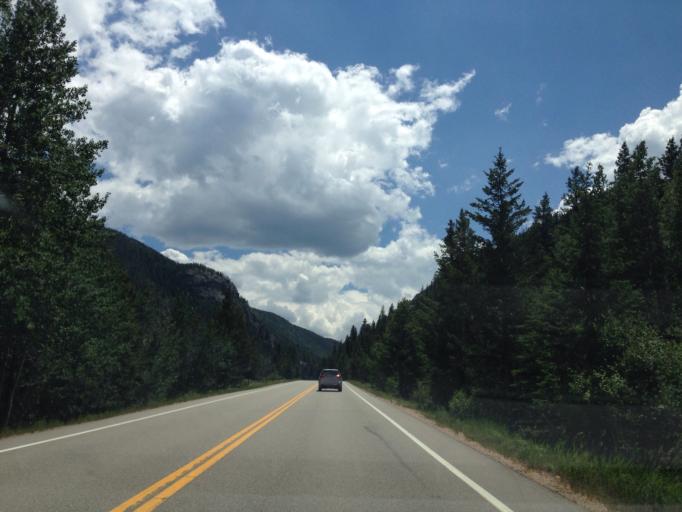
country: US
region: Colorado
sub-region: Larimer County
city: Estes Park
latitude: 40.6572
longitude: -105.8137
